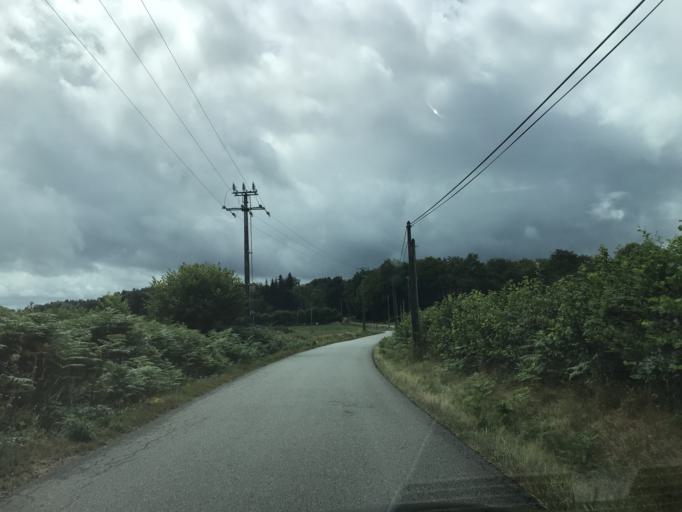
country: FR
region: Auvergne
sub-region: Departement du Cantal
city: Pleaux
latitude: 45.2561
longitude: 2.1962
